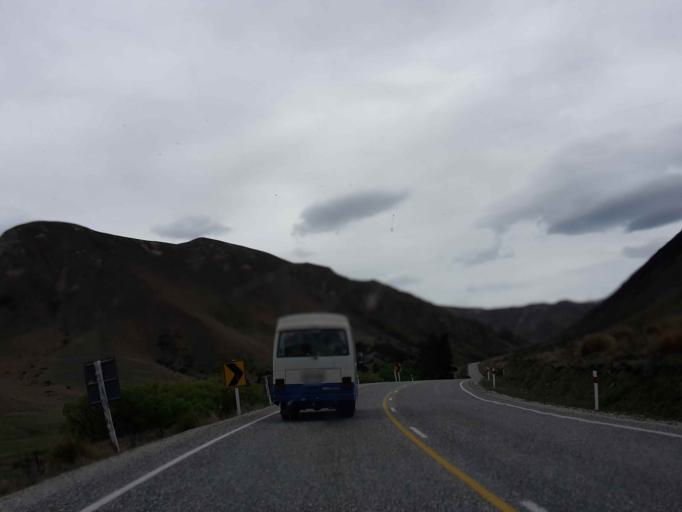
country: NZ
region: Otago
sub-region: Queenstown-Lakes District
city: Wanaka
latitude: -44.5852
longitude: 169.5846
